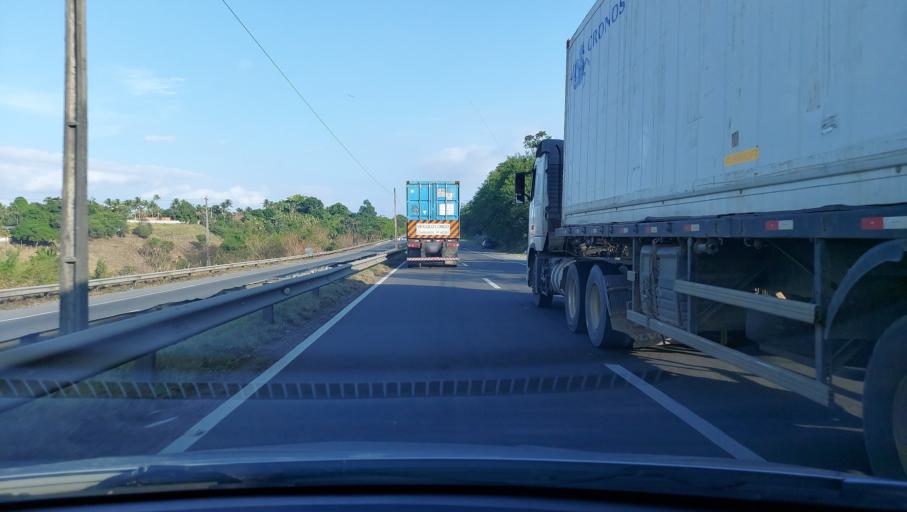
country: BR
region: Bahia
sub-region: Conceicao Do Jacuipe
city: Conceicao do Jacuipe
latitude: -12.3948
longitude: -38.7735
